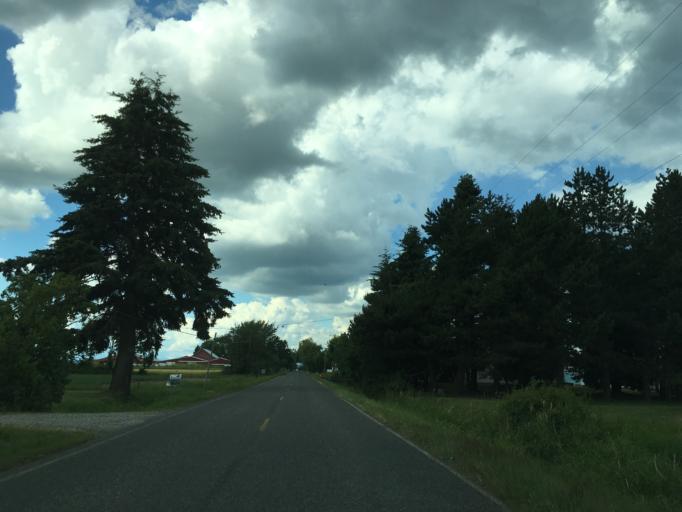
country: US
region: Washington
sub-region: Whatcom County
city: Lynden
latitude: 48.9529
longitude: -122.4744
